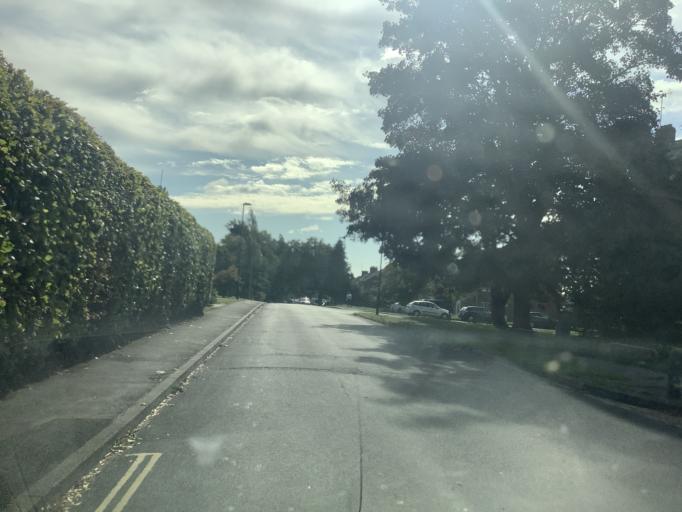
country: GB
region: England
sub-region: Hampshire
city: Marchwood
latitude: 50.9263
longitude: -1.4485
